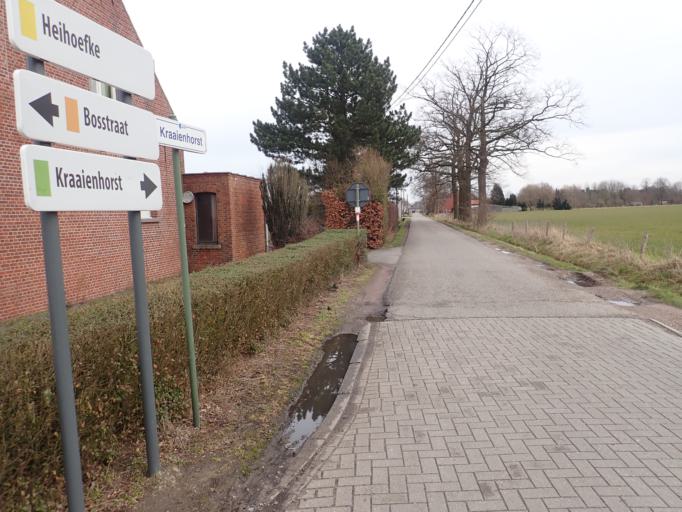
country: BE
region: Flanders
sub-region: Provincie Antwerpen
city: Brecht
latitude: 51.3391
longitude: 4.6792
